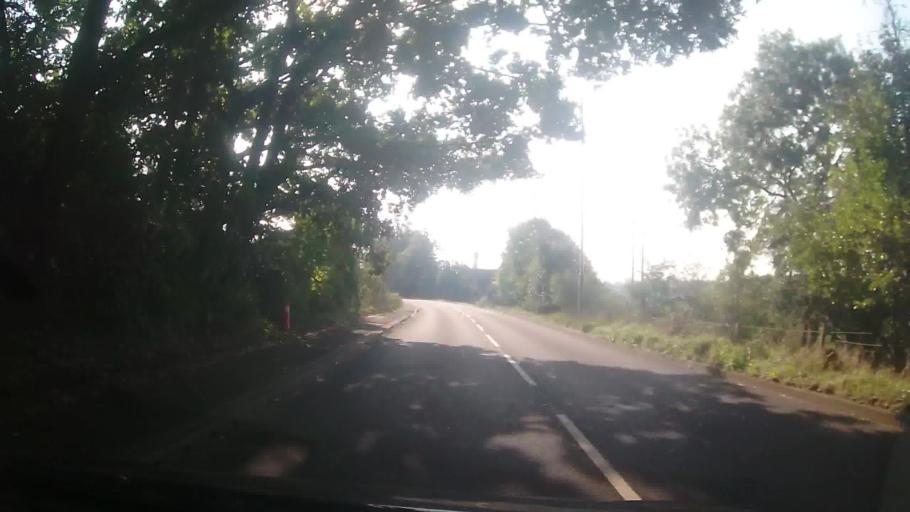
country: GB
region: England
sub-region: Shropshire
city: Bridgnorth
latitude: 52.5249
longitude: -2.4105
